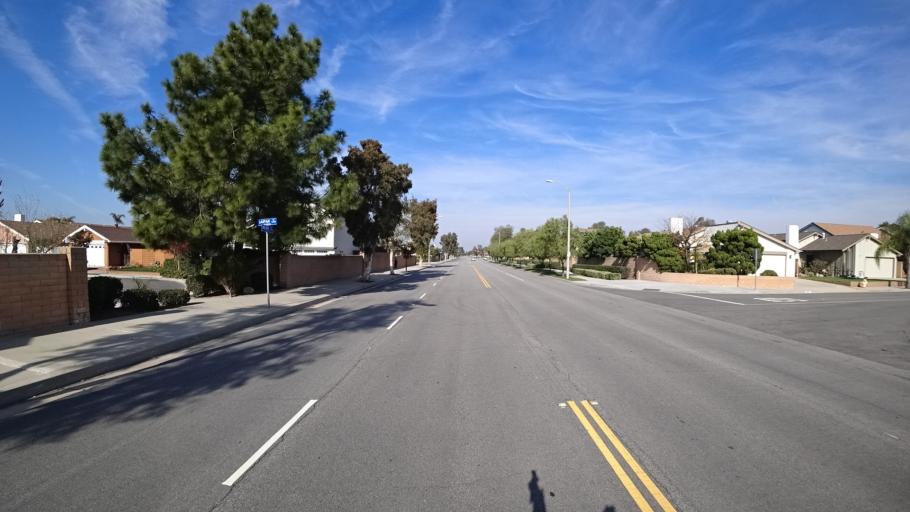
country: US
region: California
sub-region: Orange County
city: Stanton
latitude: 33.7930
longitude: -118.0198
